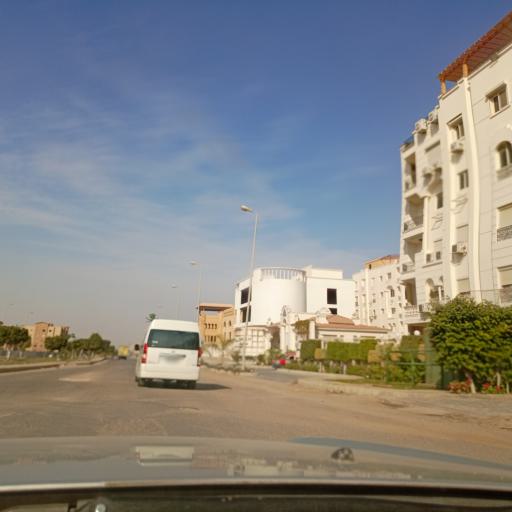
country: EG
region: Muhafazat al Qalyubiyah
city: Al Khankah
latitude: 30.0357
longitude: 31.4853
